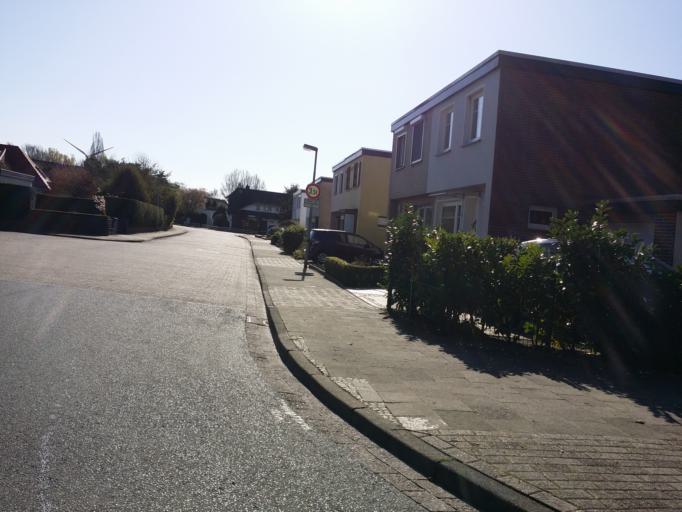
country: DE
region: Lower Saxony
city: Delmenhorst
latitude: 53.0227
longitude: 8.6614
